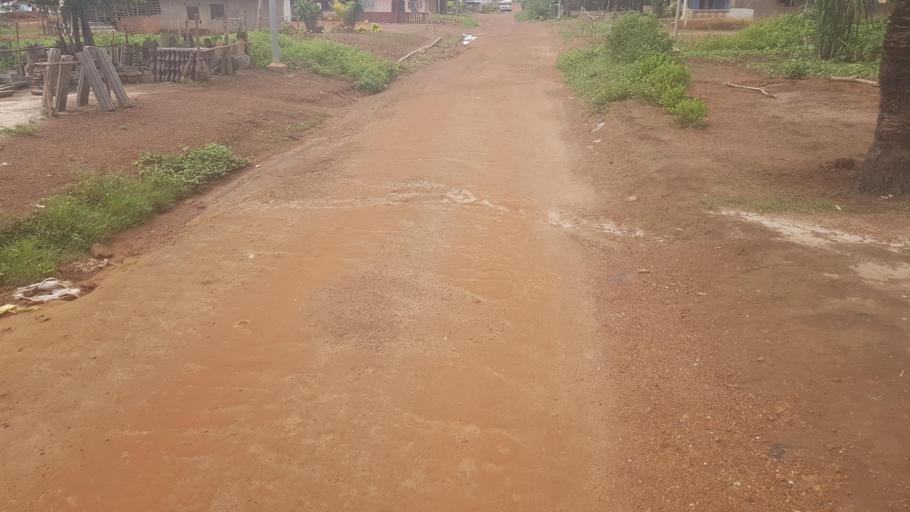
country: SL
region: Southern Province
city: Mogbwemo
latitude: 7.7590
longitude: -12.3056
